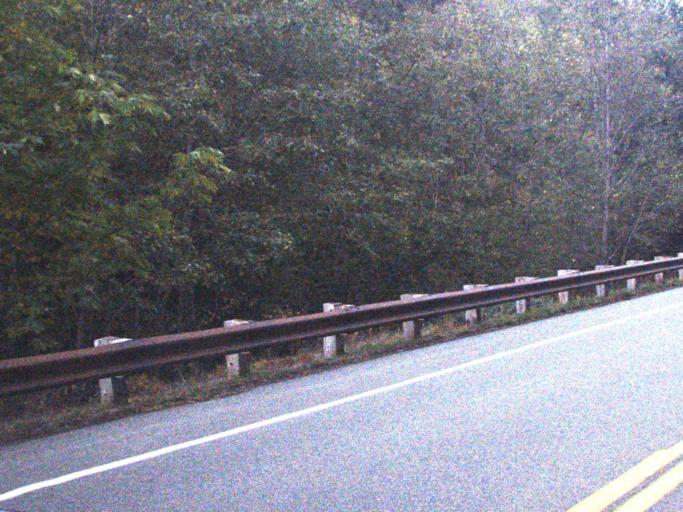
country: US
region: Washington
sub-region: Snohomish County
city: Darrington
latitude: 48.7091
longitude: -120.9823
